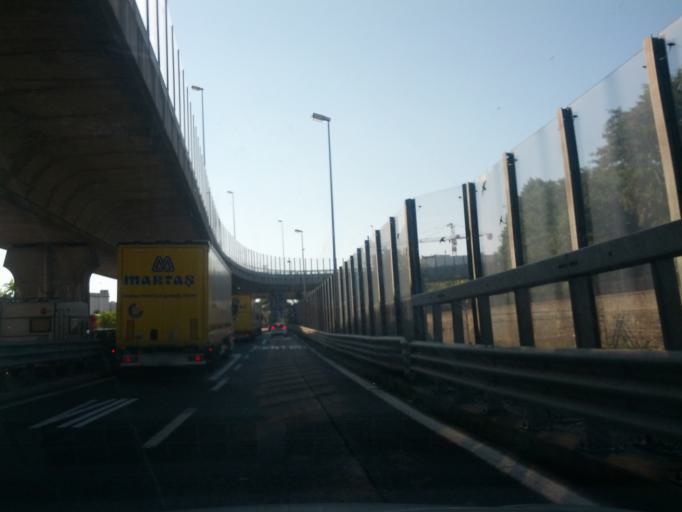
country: IT
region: Friuli Venezia Giulia
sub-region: Provincia di Trieste
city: Trieste
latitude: 45.6377
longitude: 13.7662
